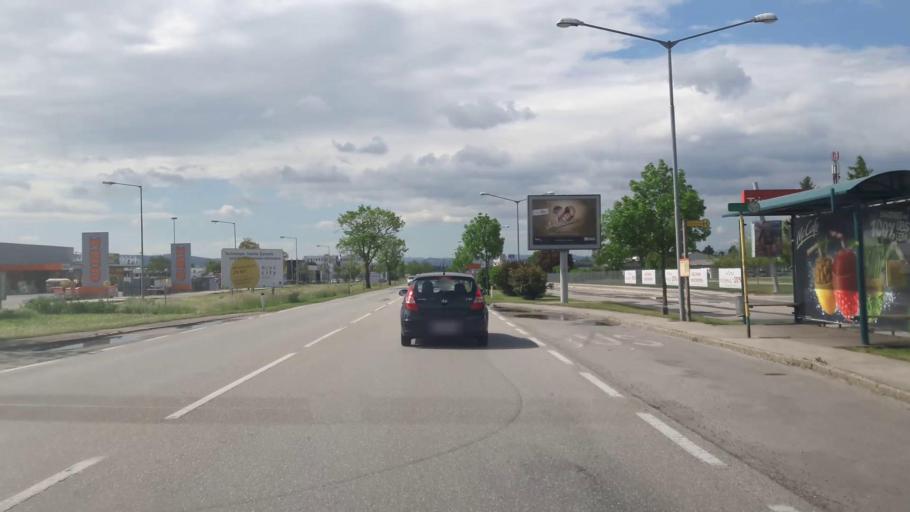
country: AT
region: Lower Austria
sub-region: Politischer Bezirk Wiener Neustadt
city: Theresienfeld
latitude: 47.8418
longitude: 16.2456
